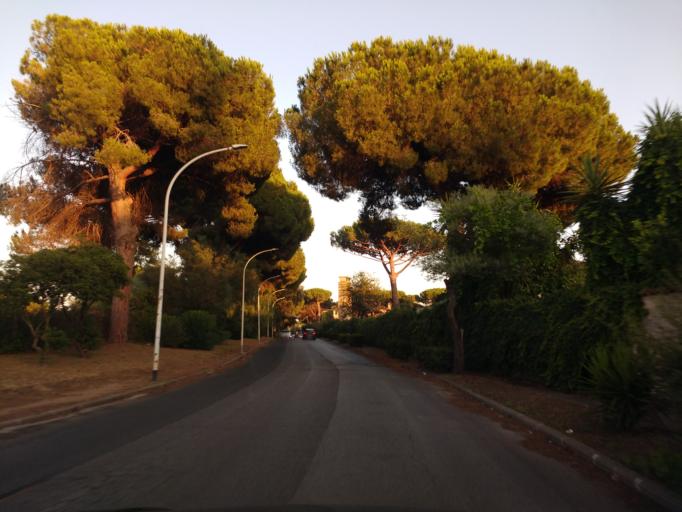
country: IT
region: Latium
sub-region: Citta metropolitana di Roma Capitale
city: Acilia-Castel Fusano-Ostia Antica
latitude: 41.7610
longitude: 12.3617
